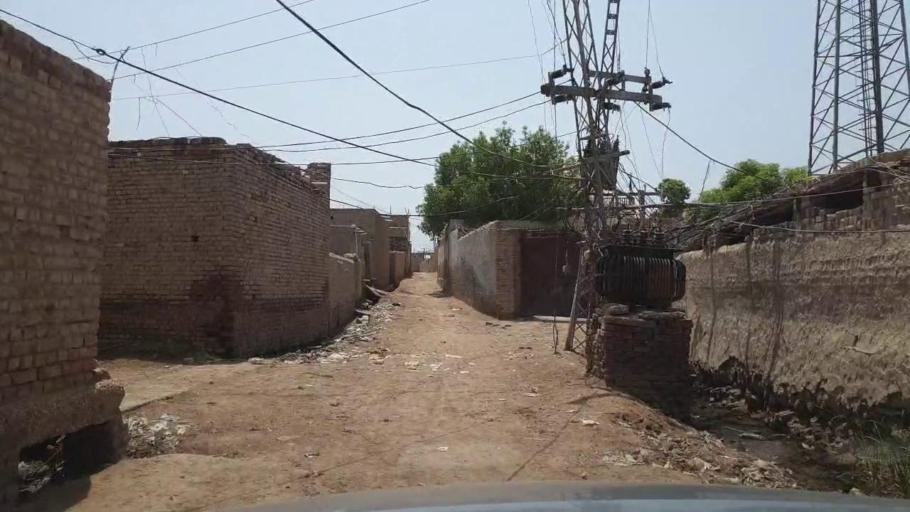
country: PK
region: Sindh
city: Madeji
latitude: 27.7614
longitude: 68.3831
